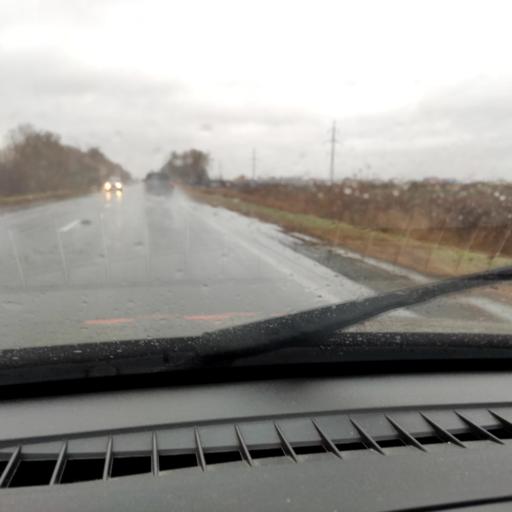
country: RU
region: Samara
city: Tol'yatti
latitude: 53.6219
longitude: 49.3088
